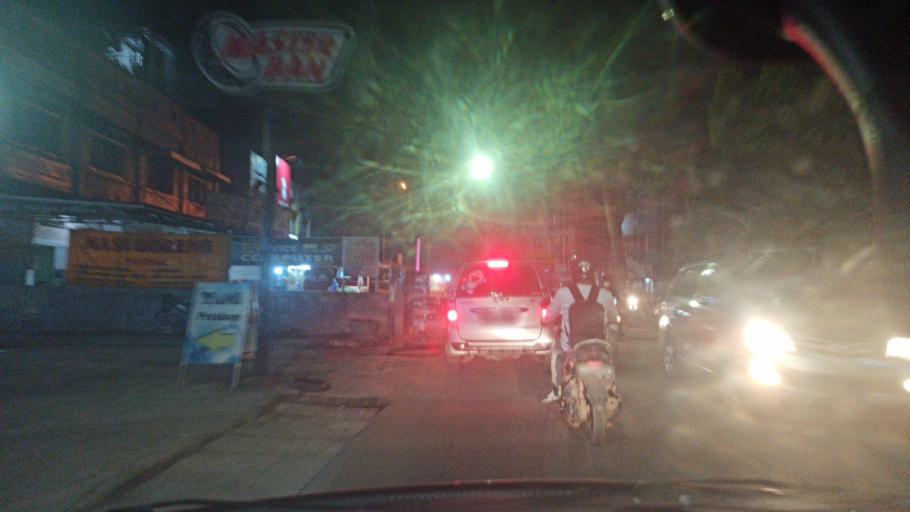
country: ID
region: South Sumatra
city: Palembang
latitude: -2.9225
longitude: 104.7820
